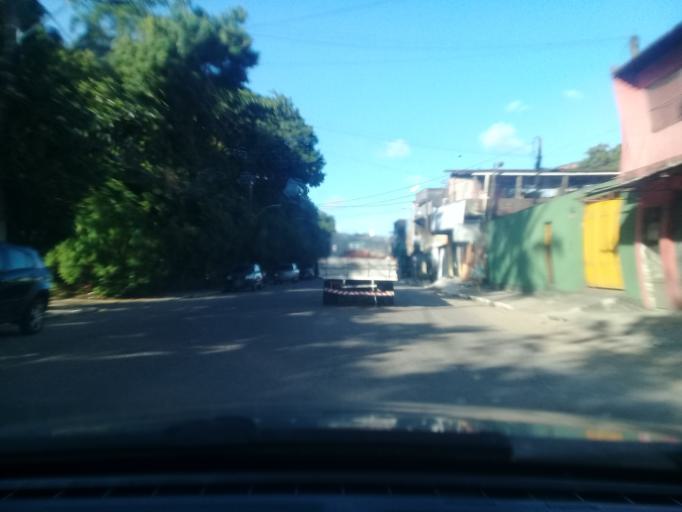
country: BR
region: Pernambuco
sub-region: Jaboatao Dos Guararapes
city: Jaboatao dos Guararapes
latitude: -8.1027
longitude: -34.9734
